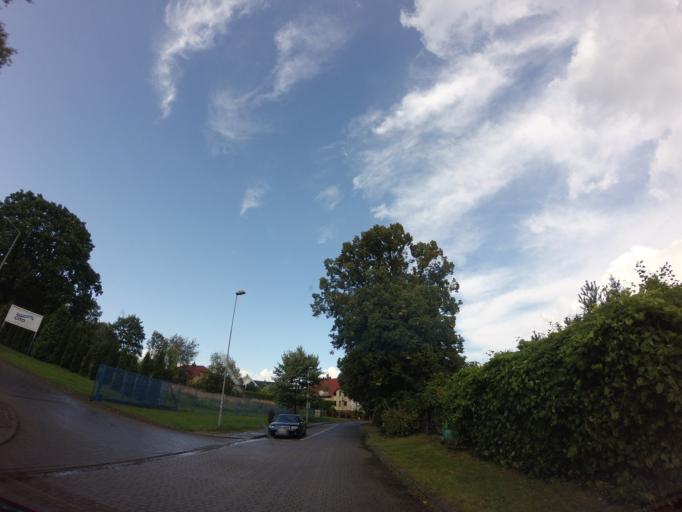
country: PL
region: West Pomeranian Voivodeship
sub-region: Szczecin
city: Szczecin
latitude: 53.4709
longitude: 14.5966
